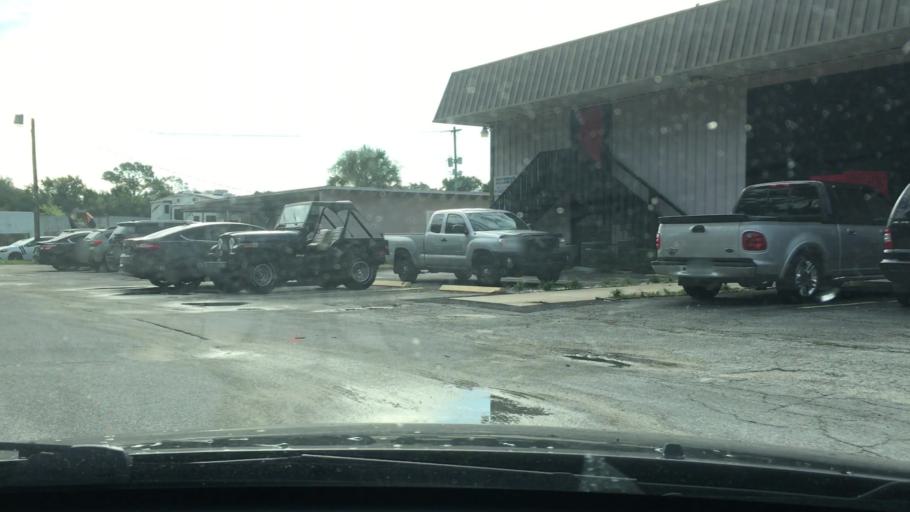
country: US
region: Florida
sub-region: Volusia County
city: Holly Hill
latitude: 29.2508
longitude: -81.0489
